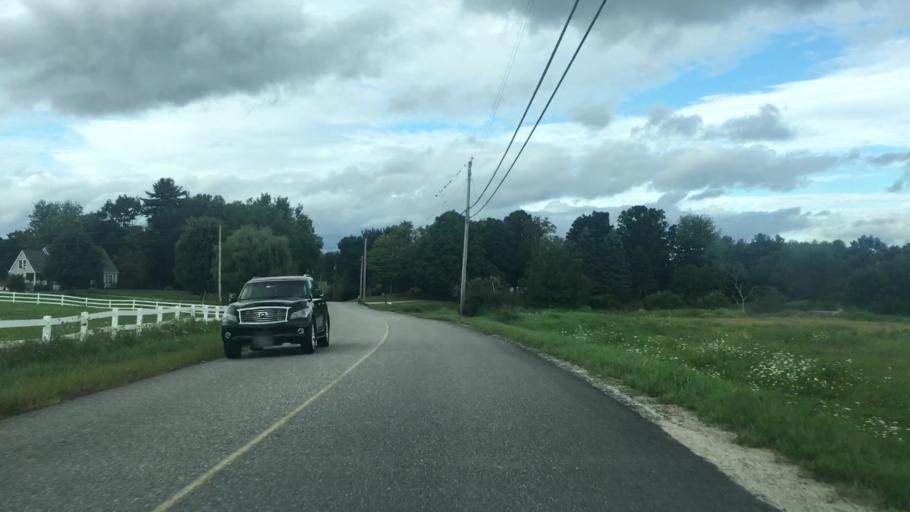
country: US
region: Maine
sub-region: York County
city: Dayton
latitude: 43.5374
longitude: -70.5784
